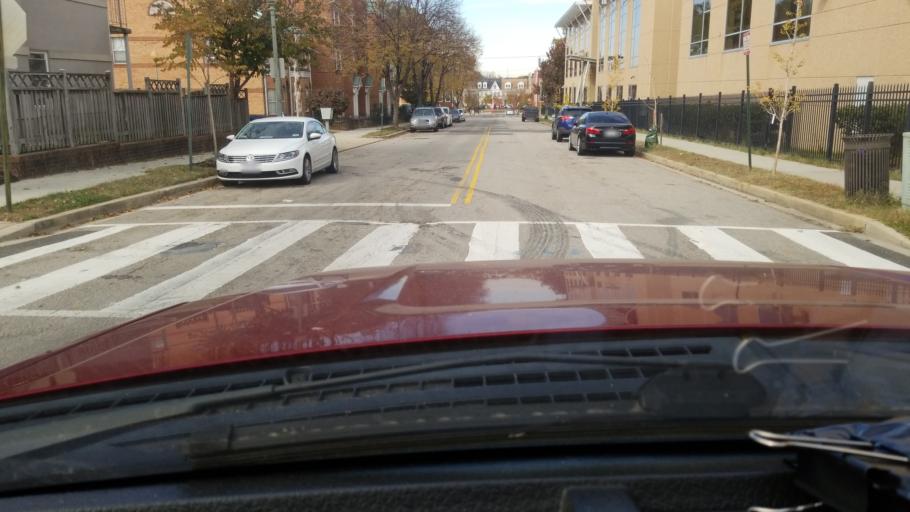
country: US
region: Maryland
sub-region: Prince George's County
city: Colmar Manor
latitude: 38.9009
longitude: -76.9489
